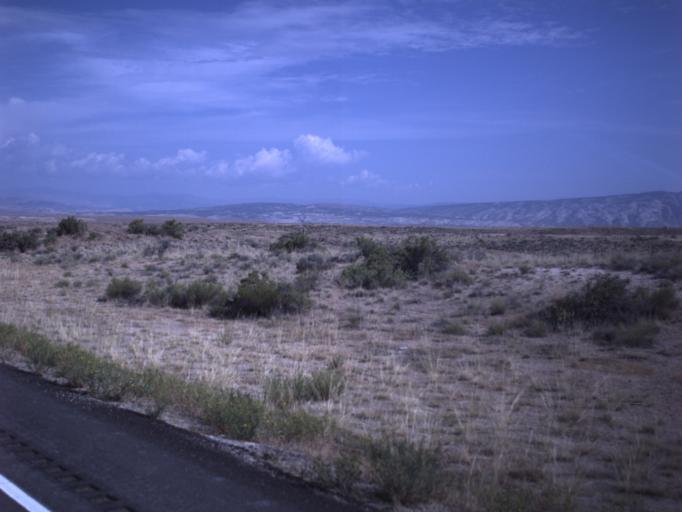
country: US
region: Utah
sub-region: Uintah County
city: Naples
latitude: 40.3396
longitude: -109.2945
